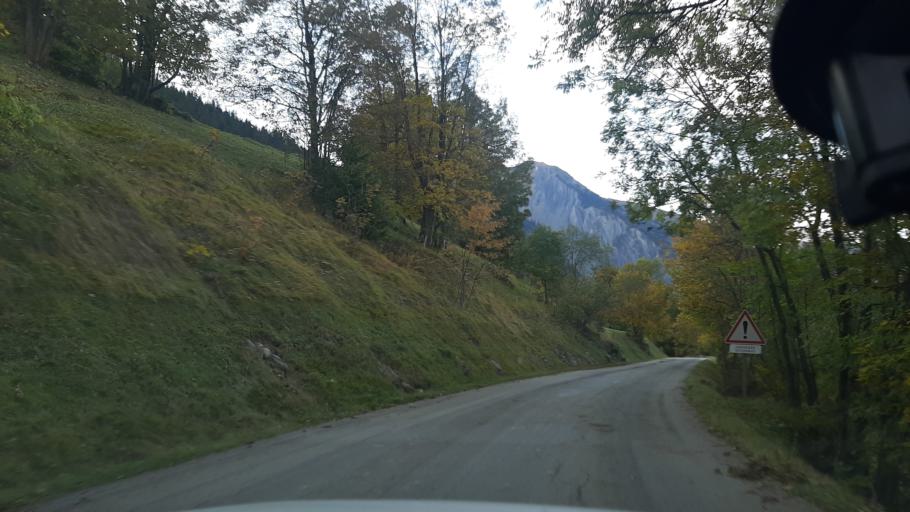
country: FR
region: Rhone-Alpes
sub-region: Departement de la Savoie
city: Villargondran
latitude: 45.1963
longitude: 6.3261
